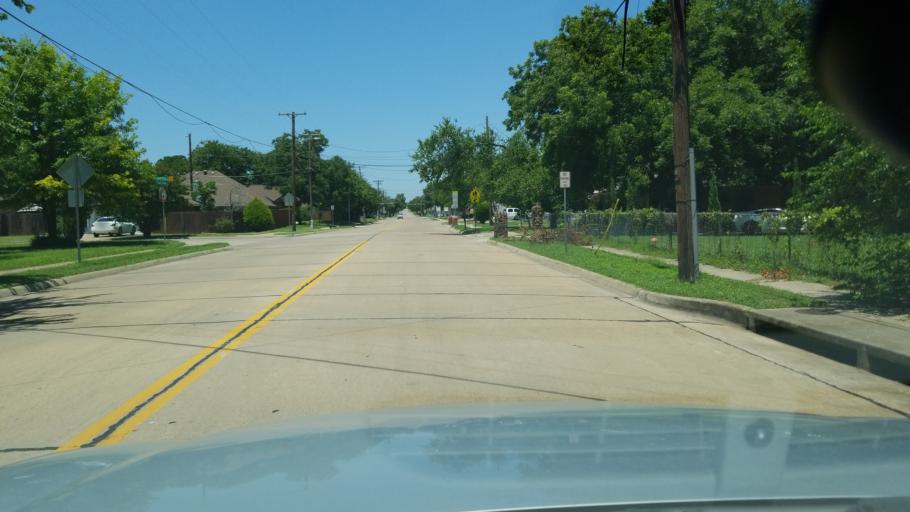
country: US
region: Texas
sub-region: Dallas County
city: Irving
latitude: 32.7984
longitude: -96.9257
